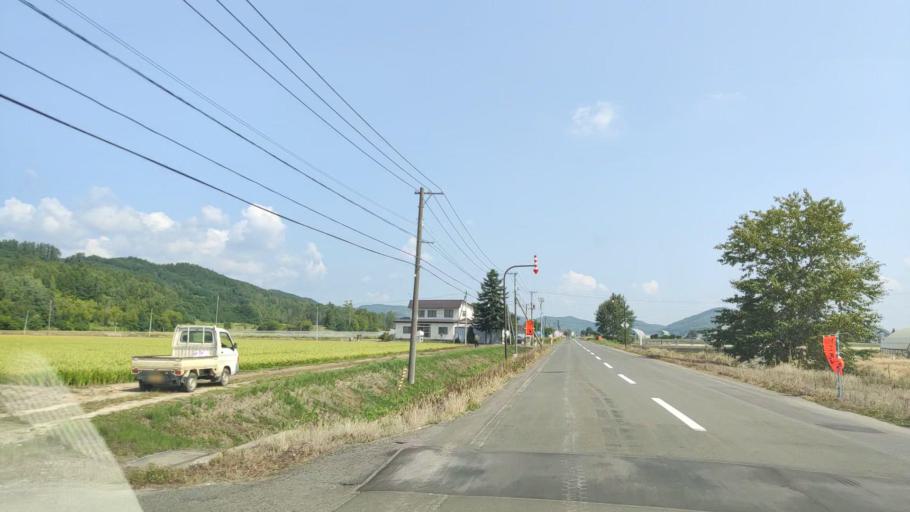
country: JP
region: Hokkaido
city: Shimo-furano
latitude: 43.3780
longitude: 142.3902
